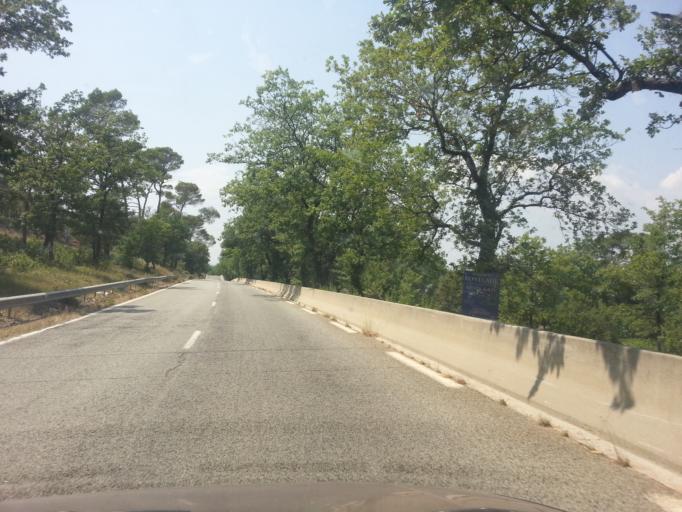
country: FR
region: Provence-Alpes-Cote d'Azur
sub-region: Departement du Var
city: Camps-la-Source
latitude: 43.4009
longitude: 6.1229
